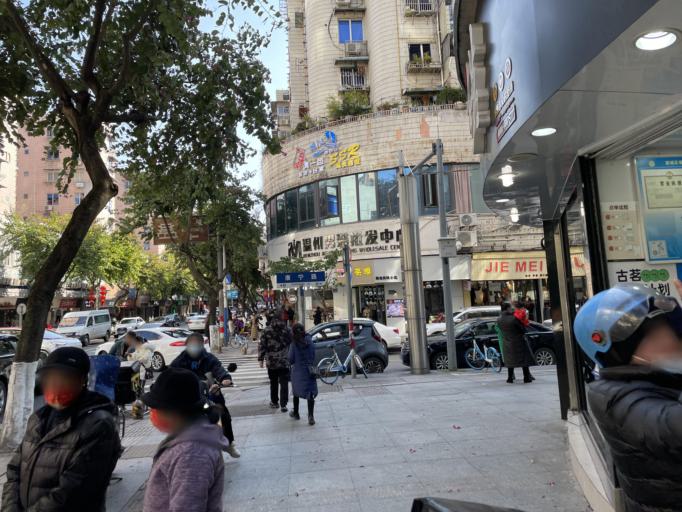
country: CN
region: Zhejiang Sheng
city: Wuma
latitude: 28.0175
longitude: 120.6528
